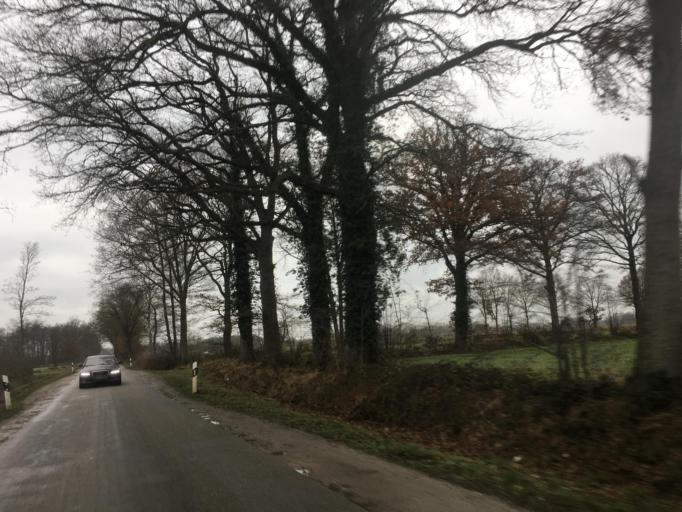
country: DE
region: North Rhine-Westphalia
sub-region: Regierungsbezirk Munster
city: Greven
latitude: 52.0748
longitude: 7.5535
